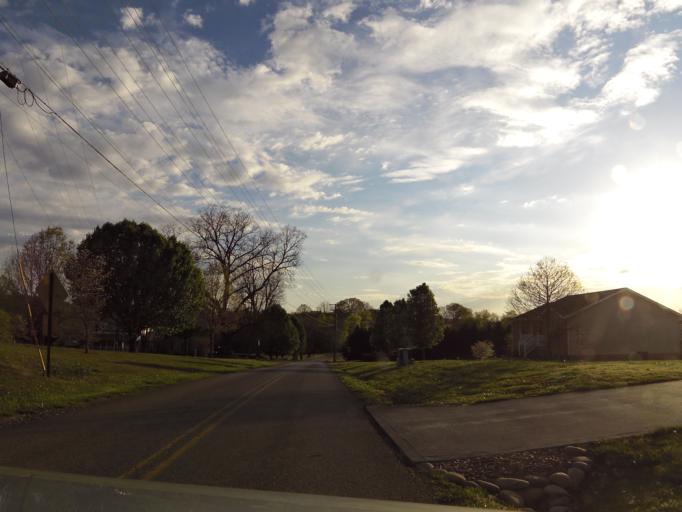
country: US
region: Tennessee
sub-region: Loudon County
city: Greenback
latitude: 35.6312
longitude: -84.0655
